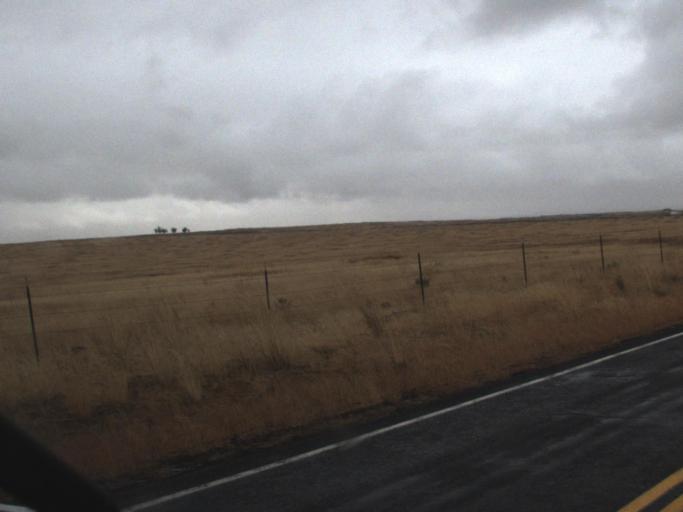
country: US
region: Washington
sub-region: Lincoln County
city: Davenport
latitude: 47.3301
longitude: -117.9833
